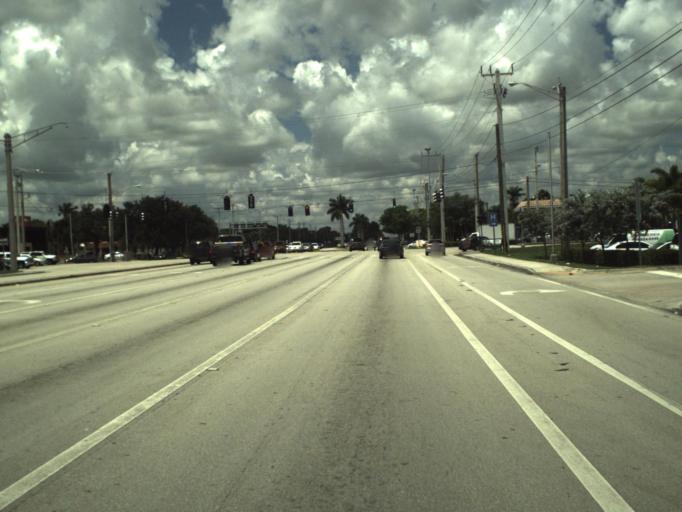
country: US
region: Florida
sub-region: Broward County
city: Pembroke Pines
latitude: 26.0093
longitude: -80.2470
